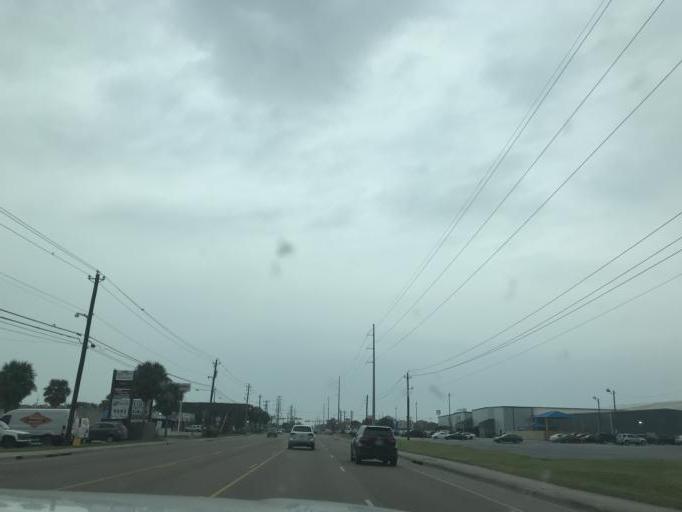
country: US
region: Texas
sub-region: Nueces County
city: Corpus Christi
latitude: 27.6934
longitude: -97.3660
